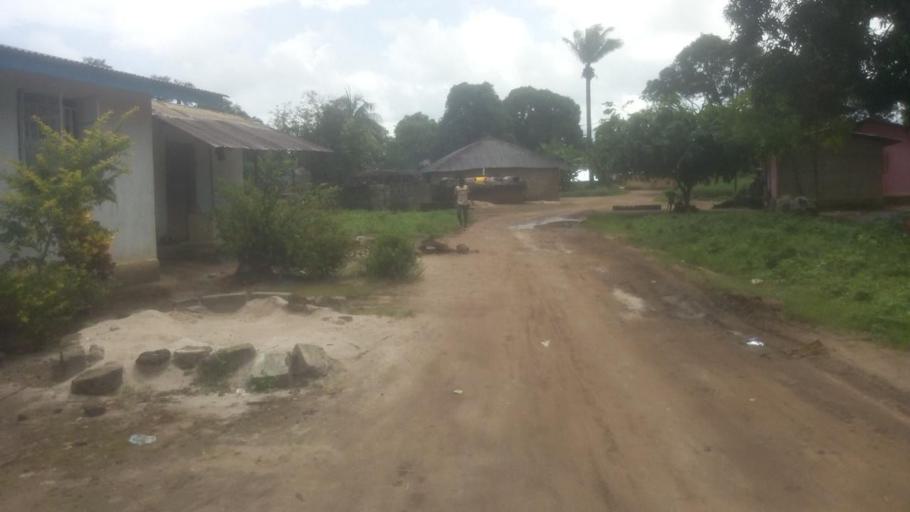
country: SL
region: Northern Province
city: Tintafor
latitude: 8.6379
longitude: -13.2205
